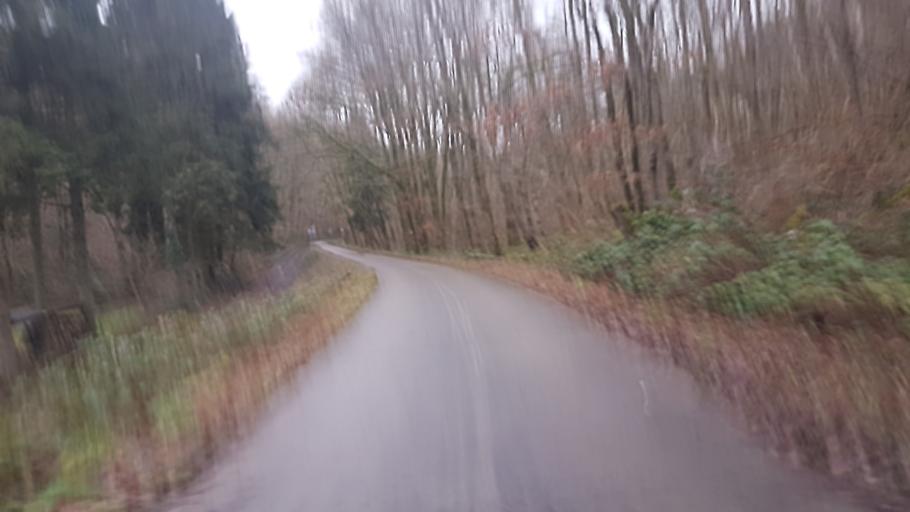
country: BE
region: Wallonia
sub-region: Province de Namur
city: Couvin
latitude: 50.0613
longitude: 4.5996
